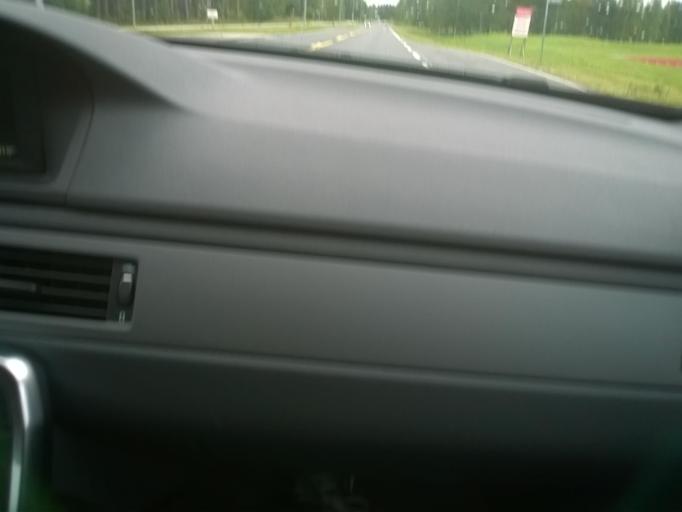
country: FI
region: Kainuu
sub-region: Kehys-Kainuu
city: Kuhmo
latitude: 64.1205
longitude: 29.5166
